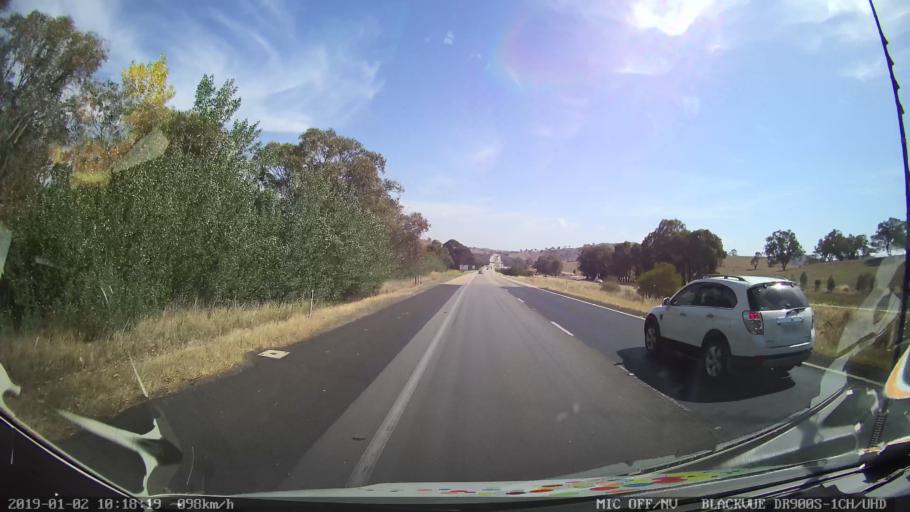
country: AU
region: New South Wales
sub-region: Gundagai
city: Gundagai
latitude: -35.0118
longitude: 148.1103
